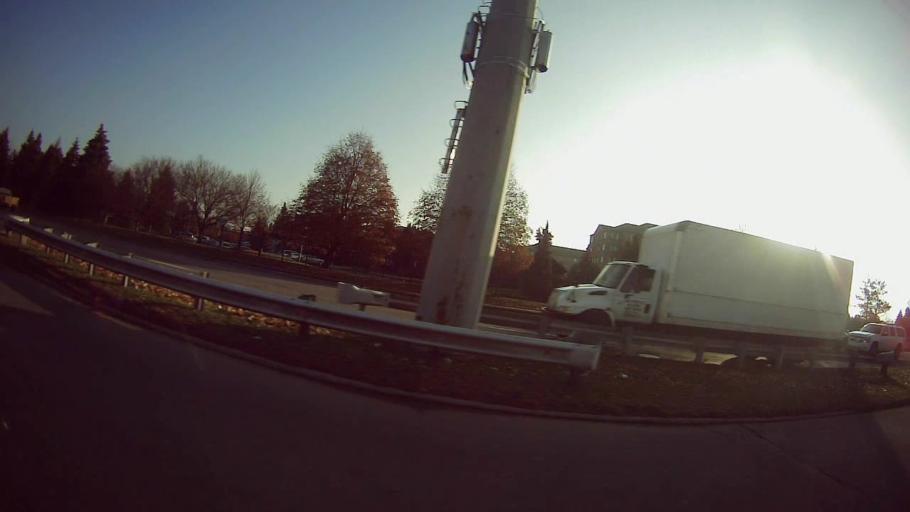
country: US
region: Michigan
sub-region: Wayne County
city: Dearborn
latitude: 42.3273
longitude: -83.1957
